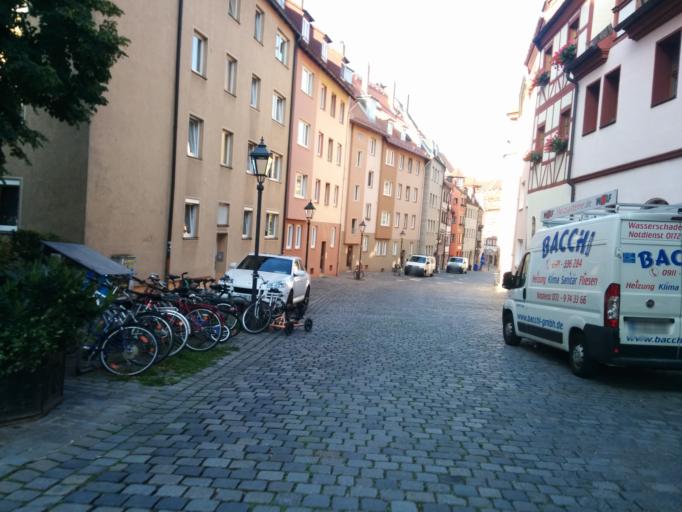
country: DE
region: Bavaria
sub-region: Regierungsbezirk Mittelfranken
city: Nuernberg
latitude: 49.4553
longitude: 11.0741
